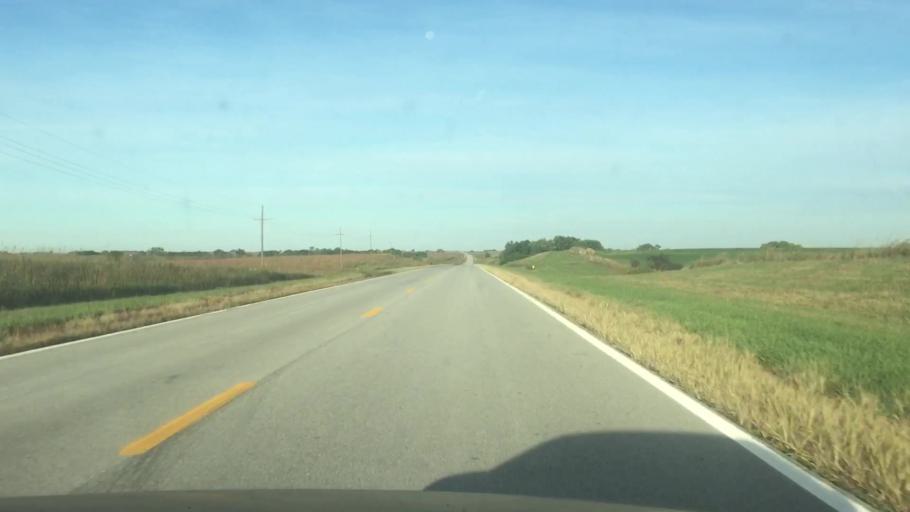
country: US
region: Nebraska
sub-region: Gage County
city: Wymore
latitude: 40.0447
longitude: -96.6724
